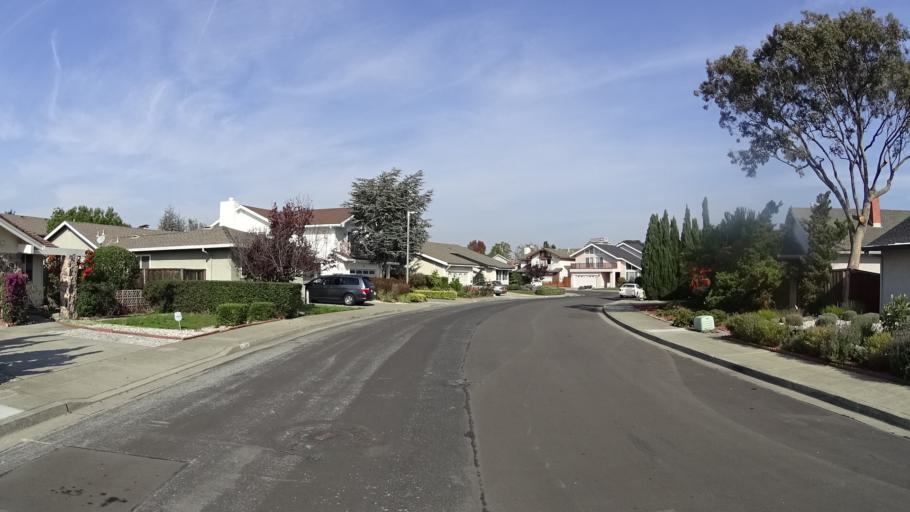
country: US
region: California
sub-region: San Mateo County
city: Foster City
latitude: 37.5483
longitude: -122.2776
